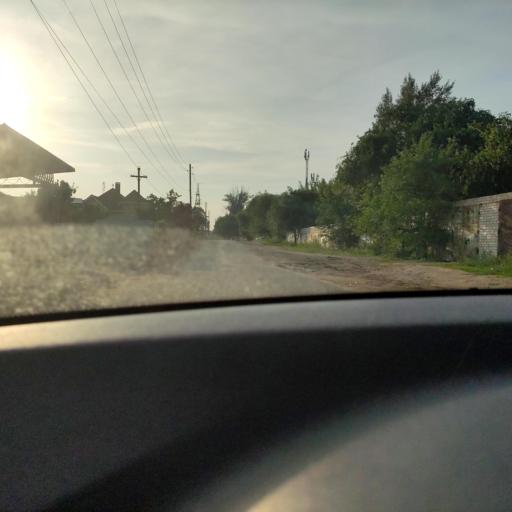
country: RU
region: Samara
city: Rozhdestveno
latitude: 53.1472
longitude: 50.0278
